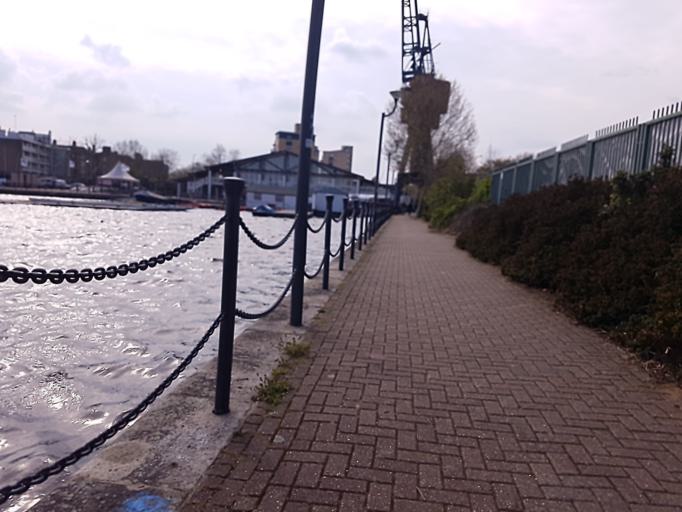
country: GB
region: England
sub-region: Greater London
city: Poplar
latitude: 51.4944
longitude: -0.0229
